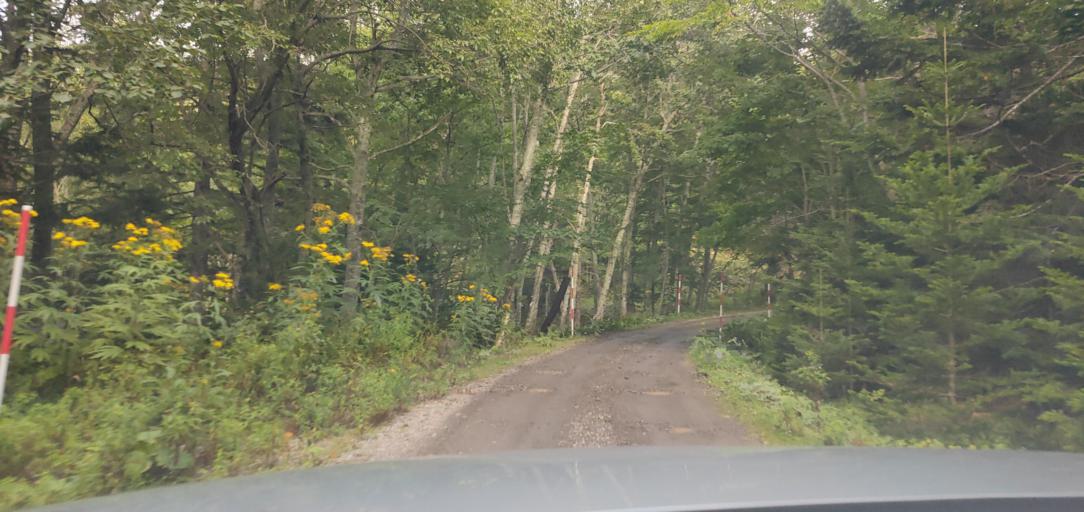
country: JP
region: Hokkaido
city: Kitami
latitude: 43.3708
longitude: 143.9463
